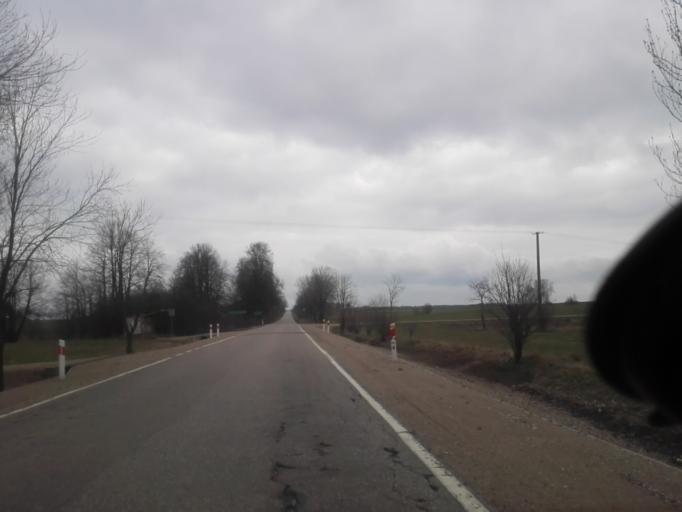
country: PL
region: Podlasie
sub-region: Suwalki
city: Suwalki
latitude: 54.2418
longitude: 22.9159
